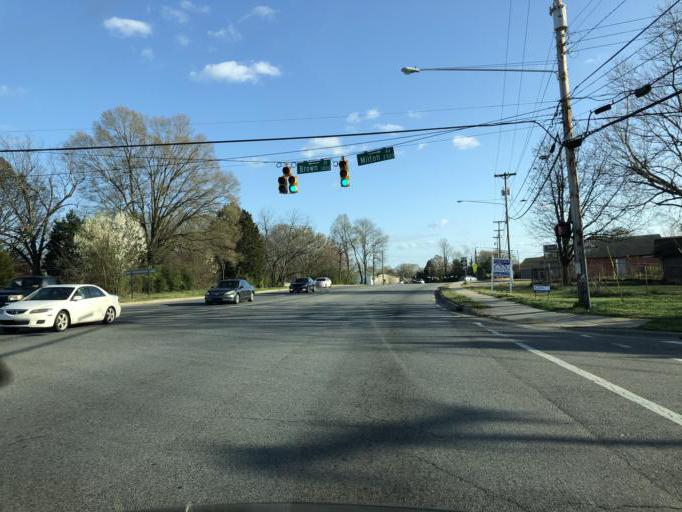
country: US
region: North Carolina
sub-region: Gaston County
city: Gastonia
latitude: 35.2705
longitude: -81.2226
